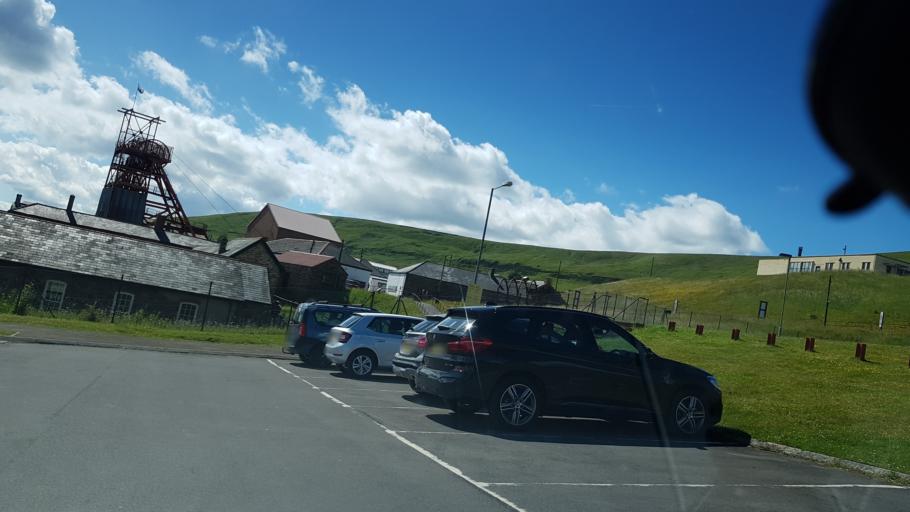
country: GB
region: Wales
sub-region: Torfaen County Borough
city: Blaenavon
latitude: 51.7733
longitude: -3.1057
